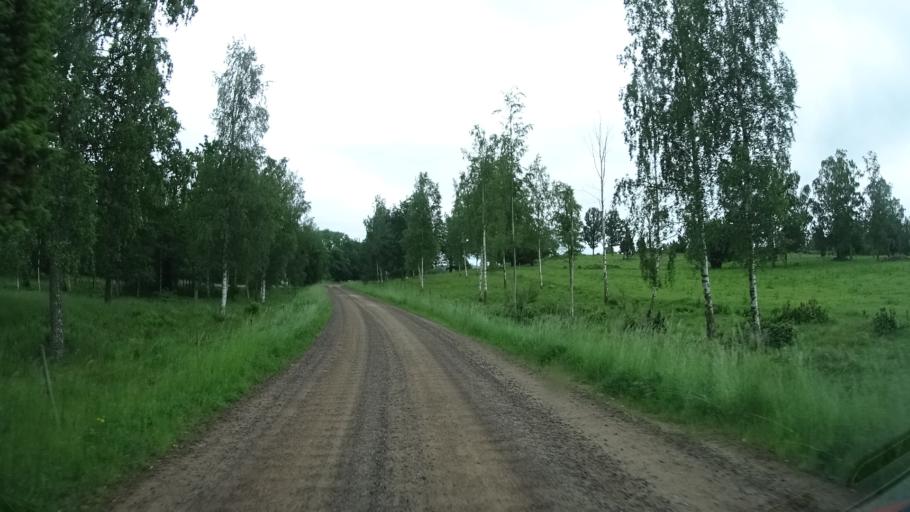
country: SE
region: Joenkoeping
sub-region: Eksjo Kommun
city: Mariannelund
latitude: 57.6151
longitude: 15.6660
